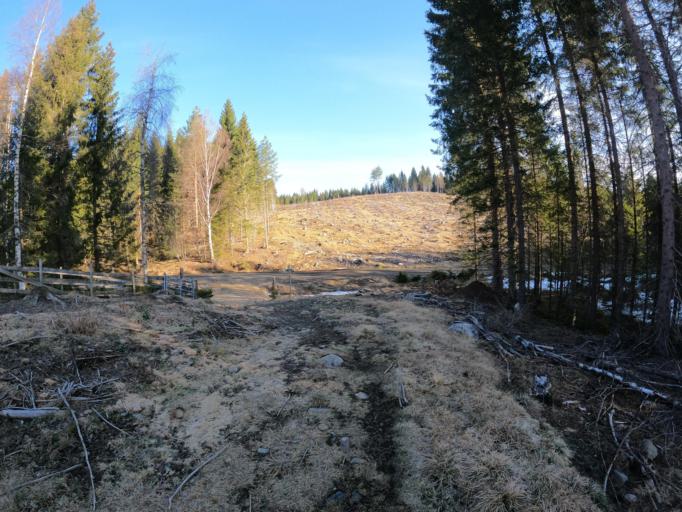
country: NO
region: Akershus
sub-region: Nittedal
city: Aneby
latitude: 60.1373
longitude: 10.9096
